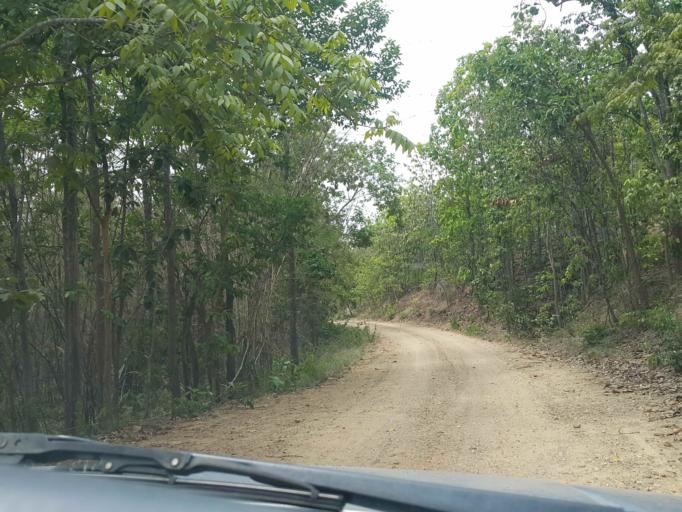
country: TH
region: Chiang Mai
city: Doi Lo
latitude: 18.5202
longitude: 98.7439
